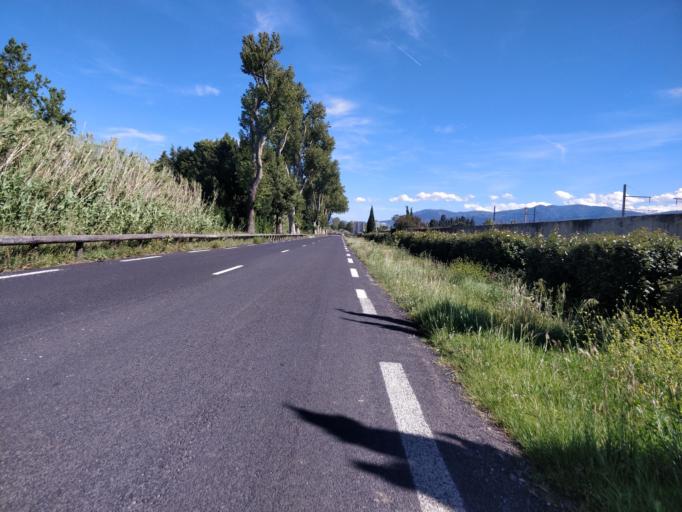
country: FR
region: Languedoc-Roussillon
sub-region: Departement des Pyrenees-Orientales
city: Corneilla-del-Vercol
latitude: 42.6205
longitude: 2.9526
